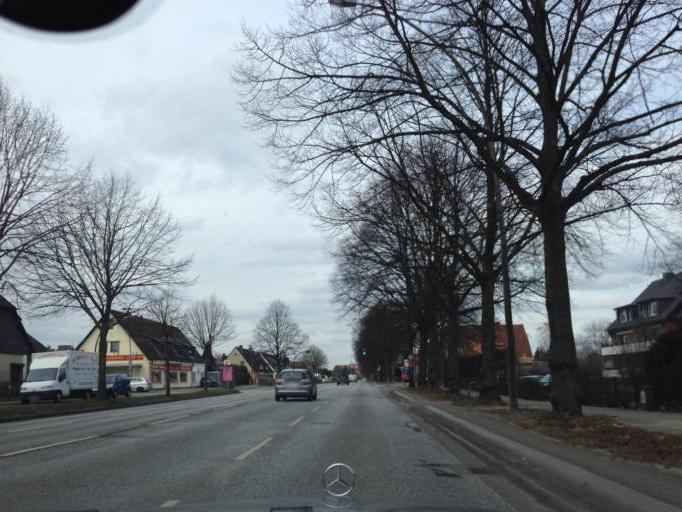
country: DE
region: Hamburg
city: Wandsbek
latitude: 53.5541
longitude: 10.1130
